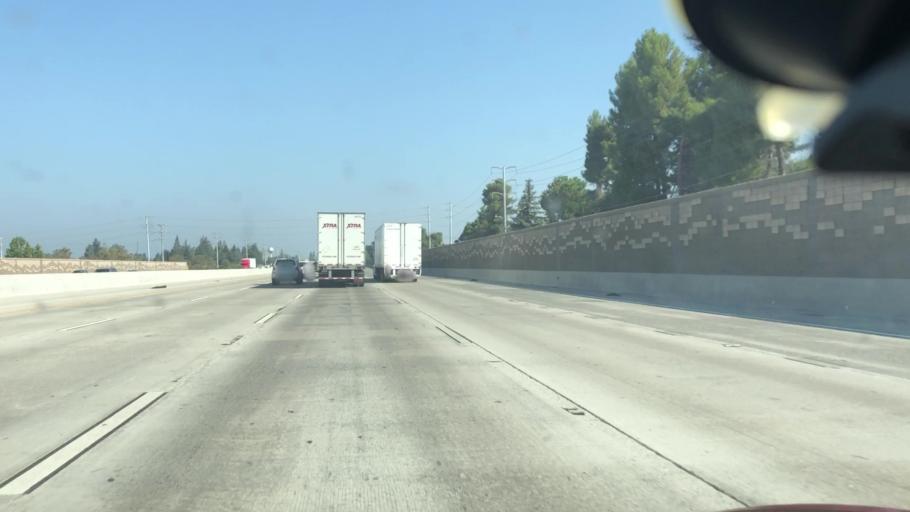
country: US
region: California
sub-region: San Joaquin County
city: Country Club
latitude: 37.9899
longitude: -121.3454
